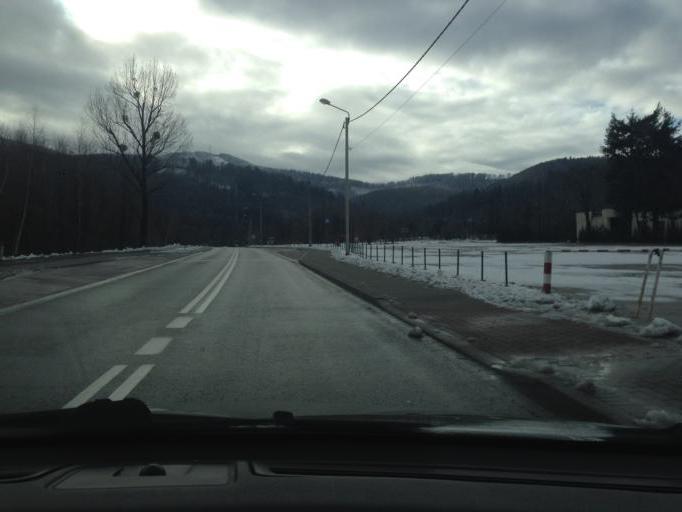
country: PL
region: Silesian Voivodeship
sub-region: Powiat bielski
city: Bystra
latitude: 49.7827
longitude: 19.0270
